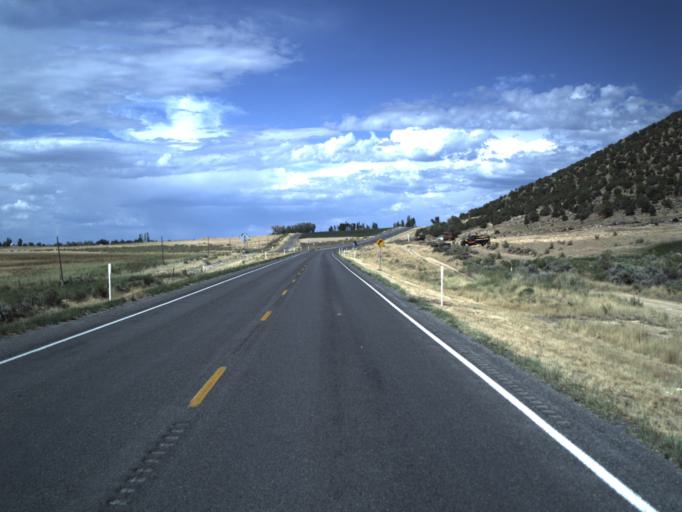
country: US
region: Utah
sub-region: Sanpete County
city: Manti
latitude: 39.2365
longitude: -111.6595
